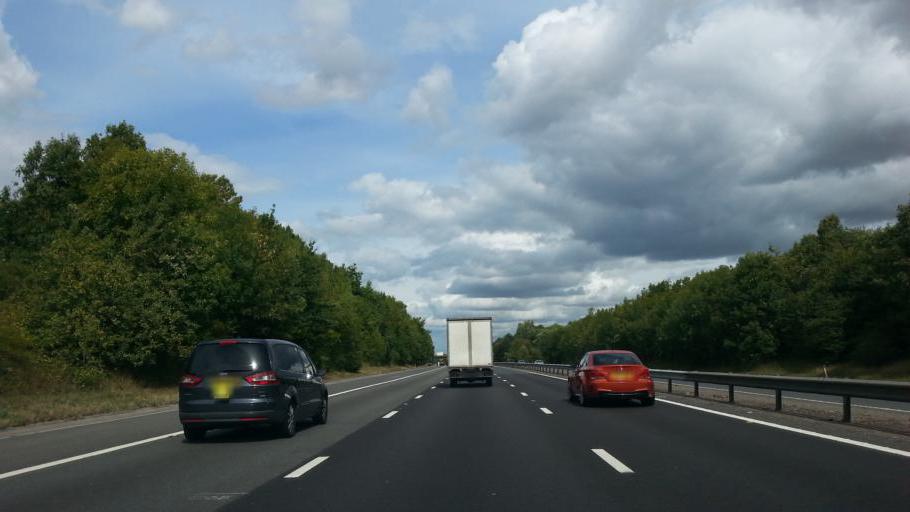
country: GB
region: England
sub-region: Hertfordshire
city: Sawbridgeworth
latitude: 51.7782
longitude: 0.1650
